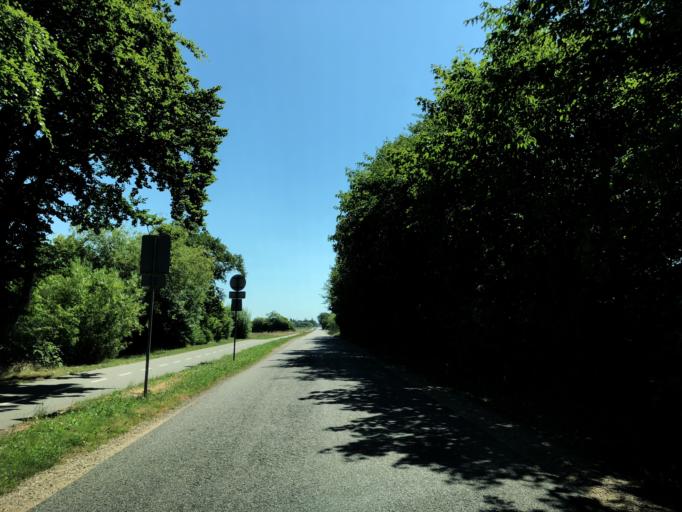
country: DK
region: Central Jutland
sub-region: Holstebro Kommune
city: Holstebro
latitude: 56.3427
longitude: 8.6717
